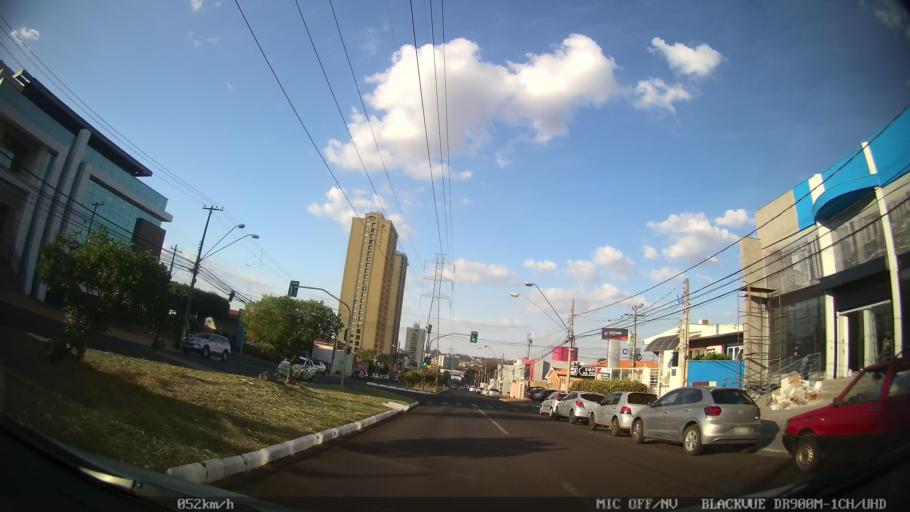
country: BR
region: Sao Paulo
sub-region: Ribeirao Preto
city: Ribeirao Preto
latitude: -21.1948
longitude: -47.8038
